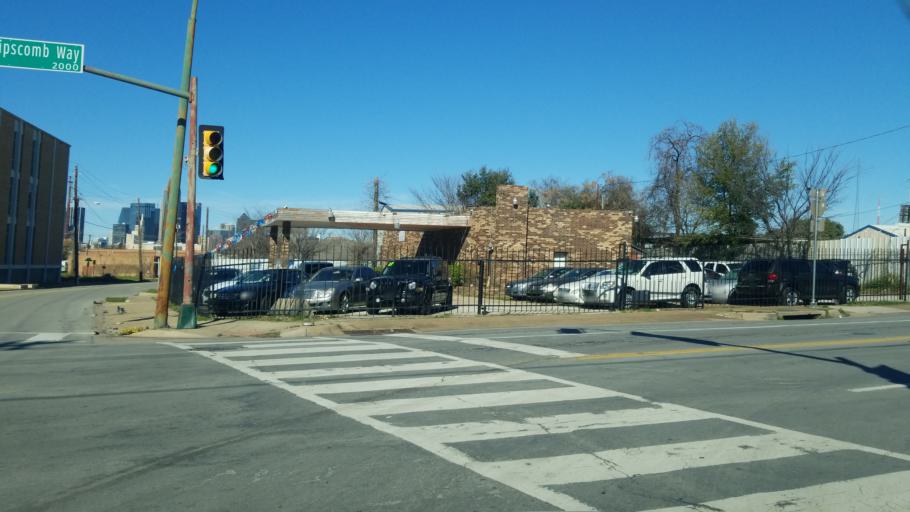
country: US
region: Texas
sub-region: Dallas County
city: Dallas
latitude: 32.7660
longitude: -96.7782
